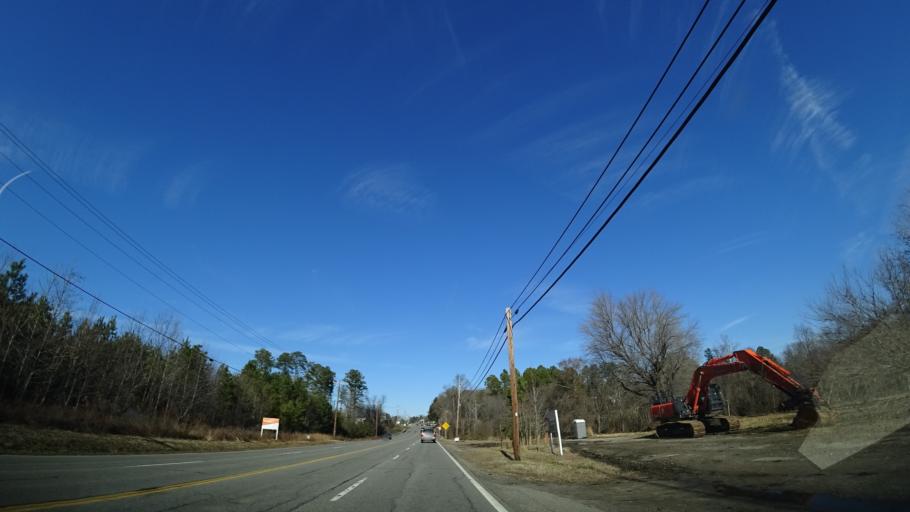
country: US
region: Virginia
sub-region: Henrico County
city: Glen Allen
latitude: 37.6939
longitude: -77.4631
